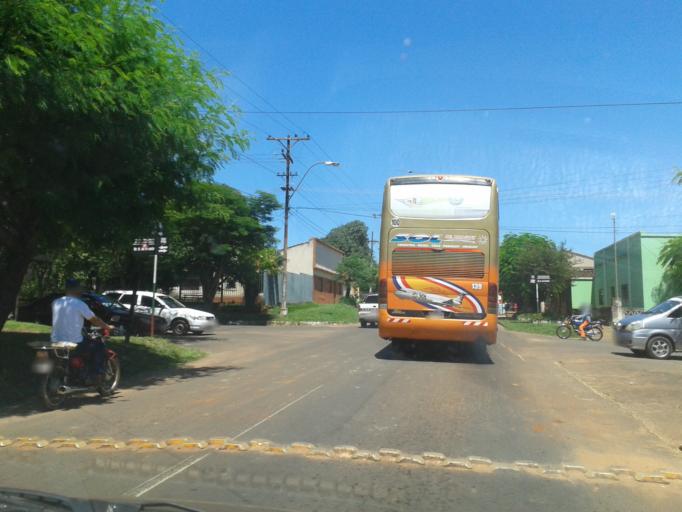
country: PY
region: Misiones
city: Santa Maria
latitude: -26.8868
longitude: -57.0180
